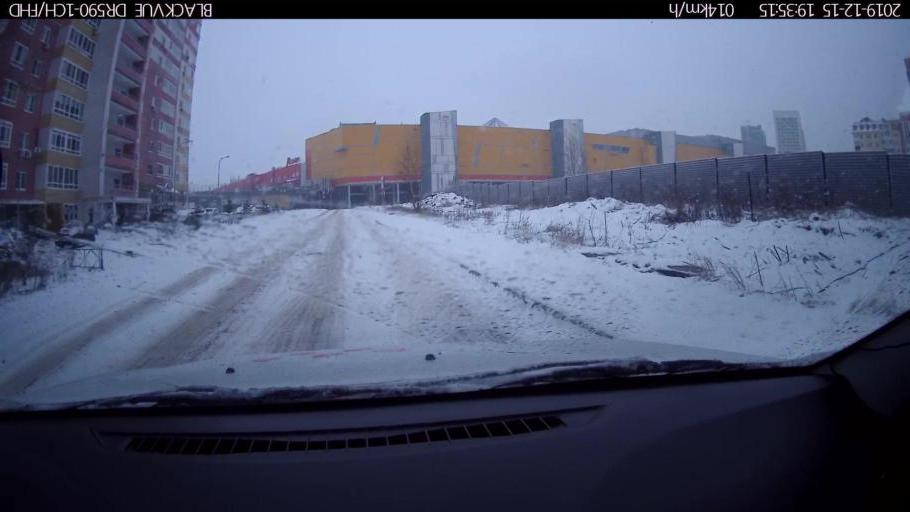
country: RU
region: Nizjnij Novgorod
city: Afonino
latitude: 56.3043
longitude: 44.0744
